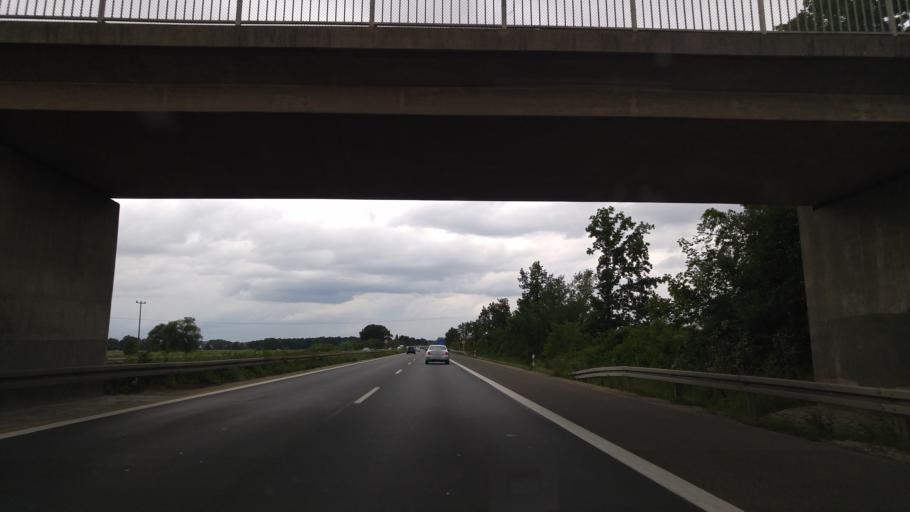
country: DE
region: Bavaria
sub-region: Regierungsbezirk Mittelfranken
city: Furth
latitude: 49.5028
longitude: 10.9967
